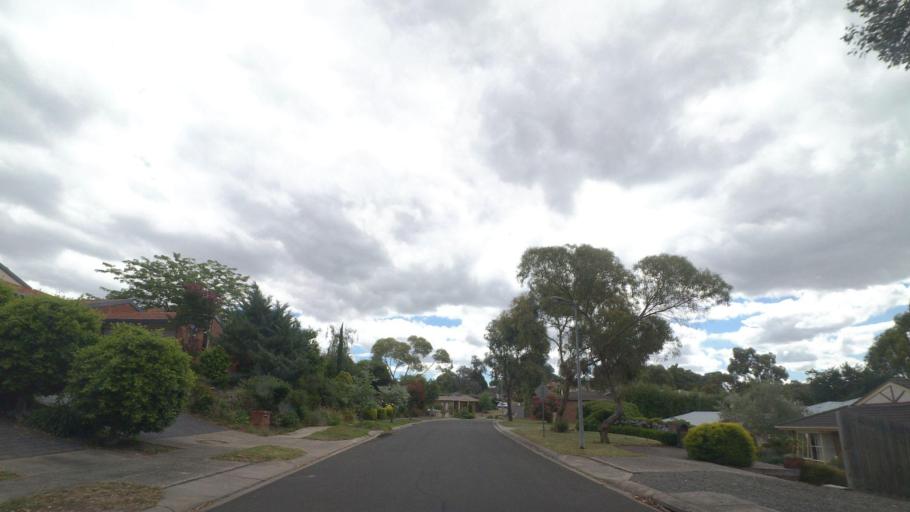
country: AU
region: Victoria
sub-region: Maroondah
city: Croydon Hills
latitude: -37.7681
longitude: 145.2567
